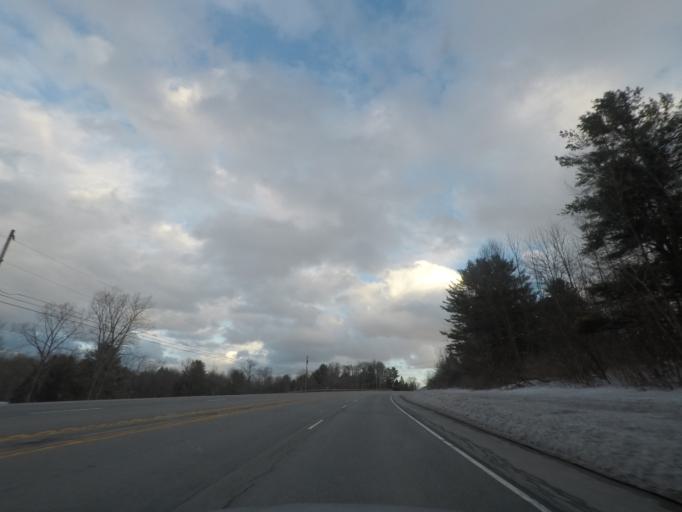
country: US
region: New York
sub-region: Herkimer County
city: Little Falls
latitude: 43.0240
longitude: -74.7859
